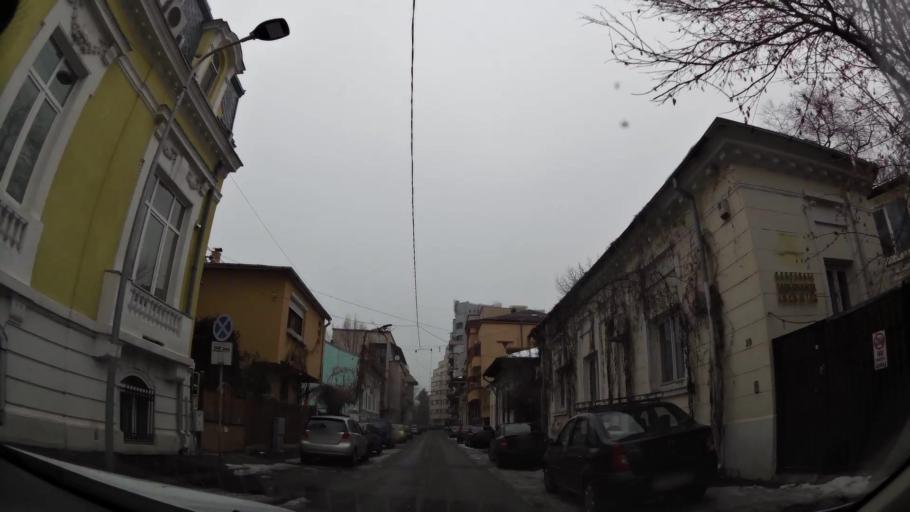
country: RO
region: Bucuresti
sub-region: Municipiul Bucuresti
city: Bucharest
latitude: 44.4410
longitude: 26.1105
